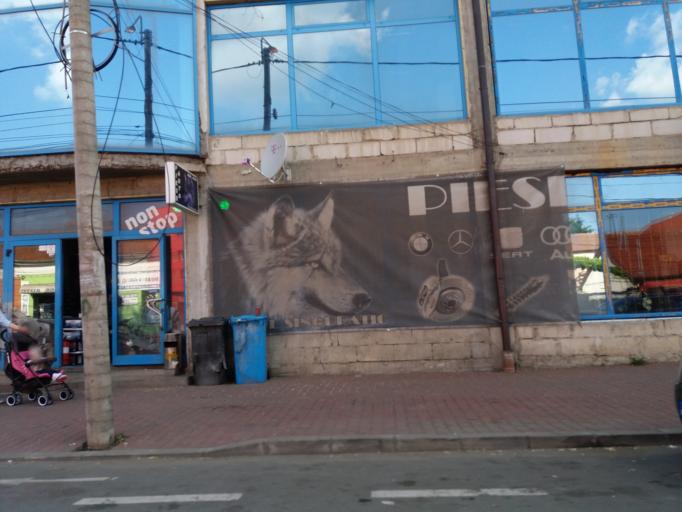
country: RO
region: Arad
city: Arad
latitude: 46.1800
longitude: 21.3087
